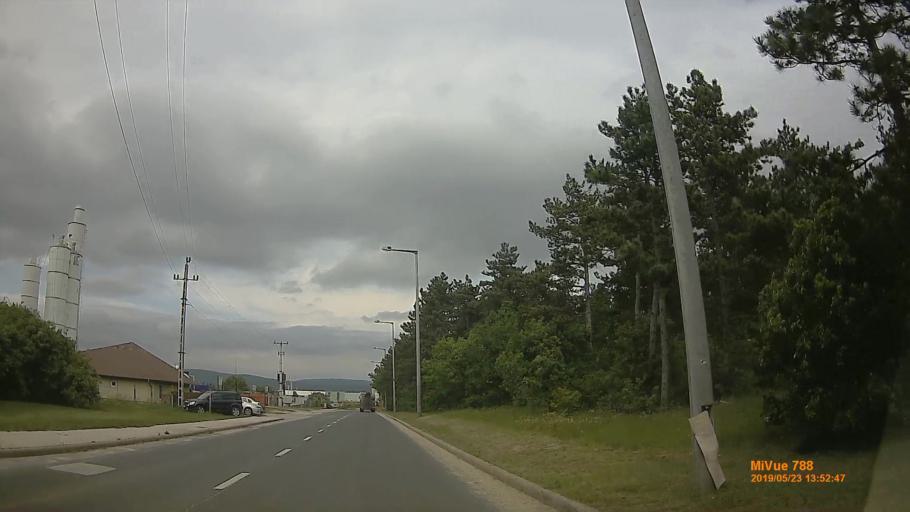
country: HU
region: Veszprem
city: Veszprem
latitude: 47.1109
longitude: 17.9009
